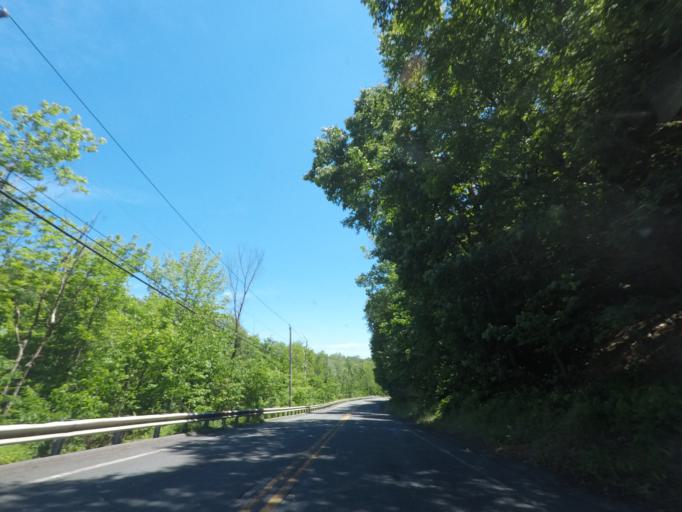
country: US
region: Massachusetts
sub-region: Berkshire County
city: Becket
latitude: 42.2621
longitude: -72.9611
